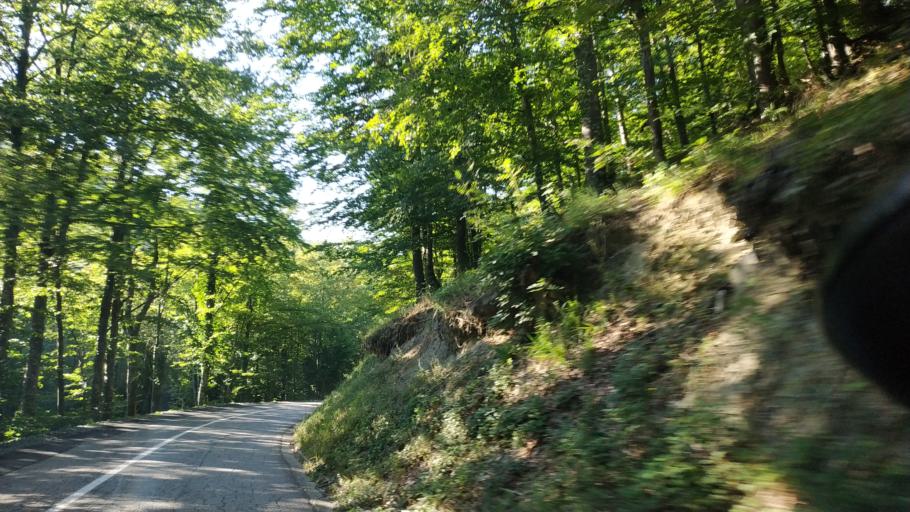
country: RS
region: Central Serbia
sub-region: Rasinski Okrug
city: Krusevac
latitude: 43.4503
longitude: 21.3604
